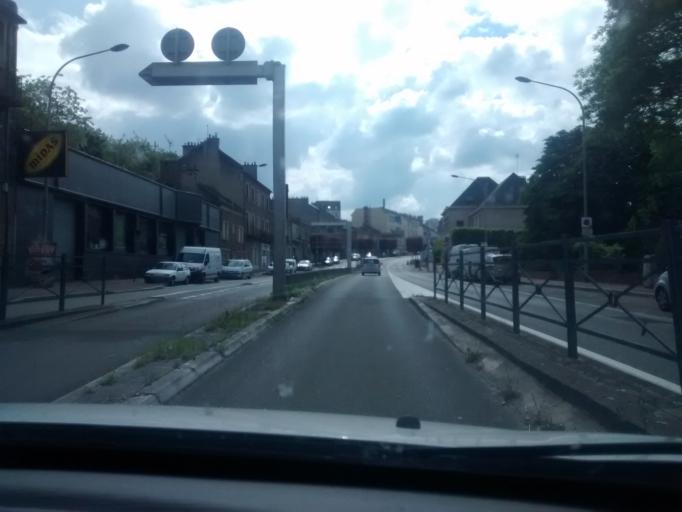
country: FR
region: Ile-de-France
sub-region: Departement des Yvelines
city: Saint-Cyr-l'Ecole
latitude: 48.7988
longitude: 2.0688
